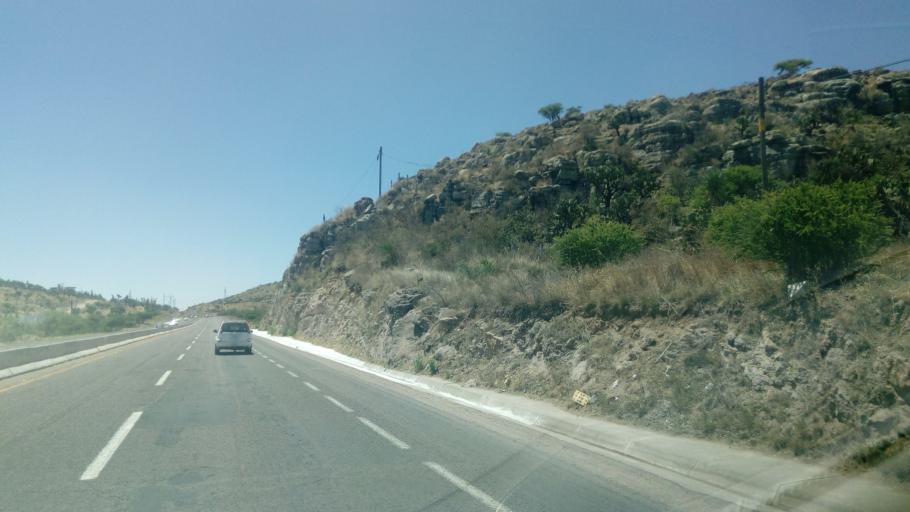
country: MX
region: Durango
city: Victoria de Durango
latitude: 24.0944
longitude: -104.6847
